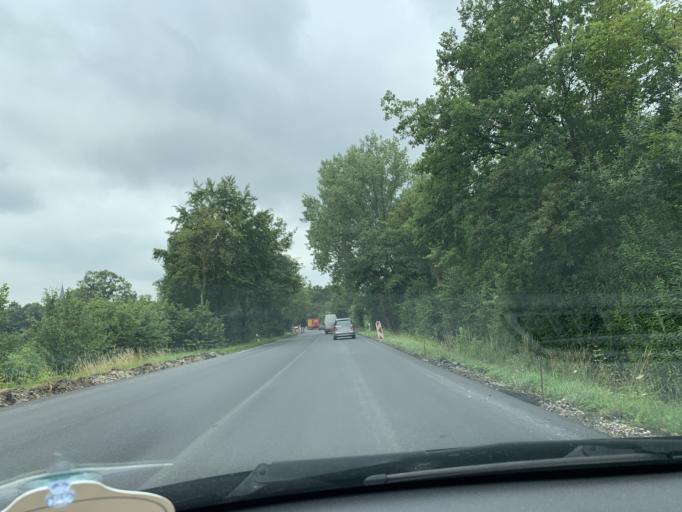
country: DE
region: North Rhine-Westphalia
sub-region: Regierungsbezirk Munster
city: Ennigerloh
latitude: 51.8905
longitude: 8.0471
